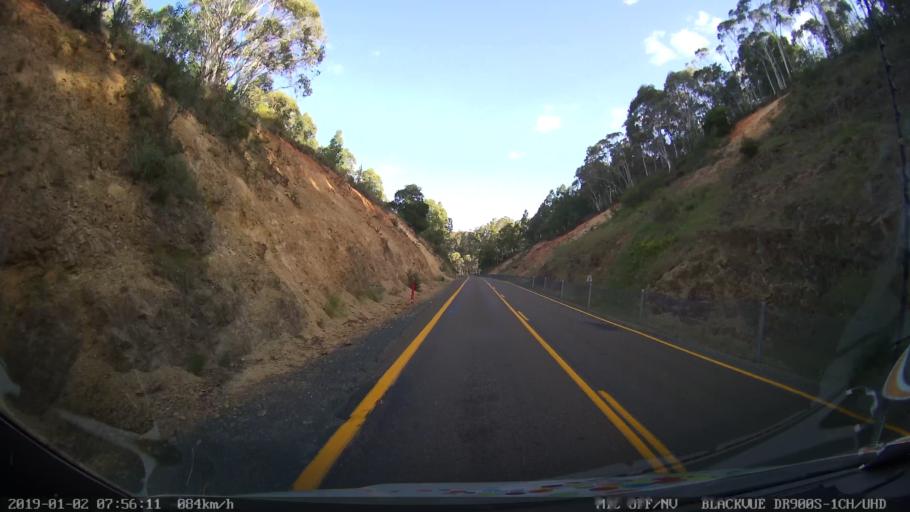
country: AU
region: New South Wales
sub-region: Tumut Shire
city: Tumut
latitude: -35.6738
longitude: 148.4859
